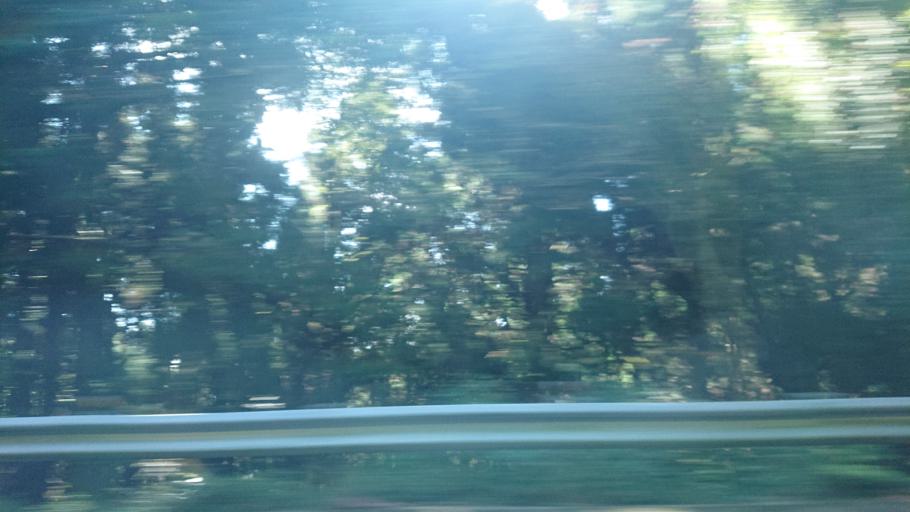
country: TW
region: Taiwan
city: Lugu
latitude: 23.5023
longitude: 120.8122
